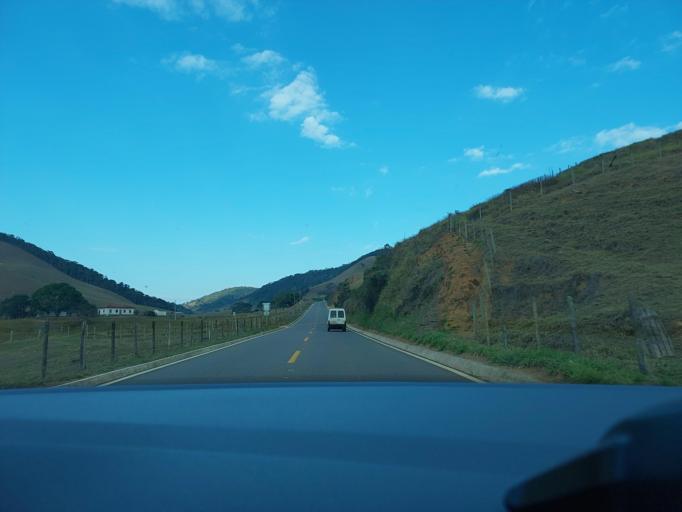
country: BR
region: Minas Gerais
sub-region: Muriae
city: Muriae
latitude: -21.0554
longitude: -42.5058
